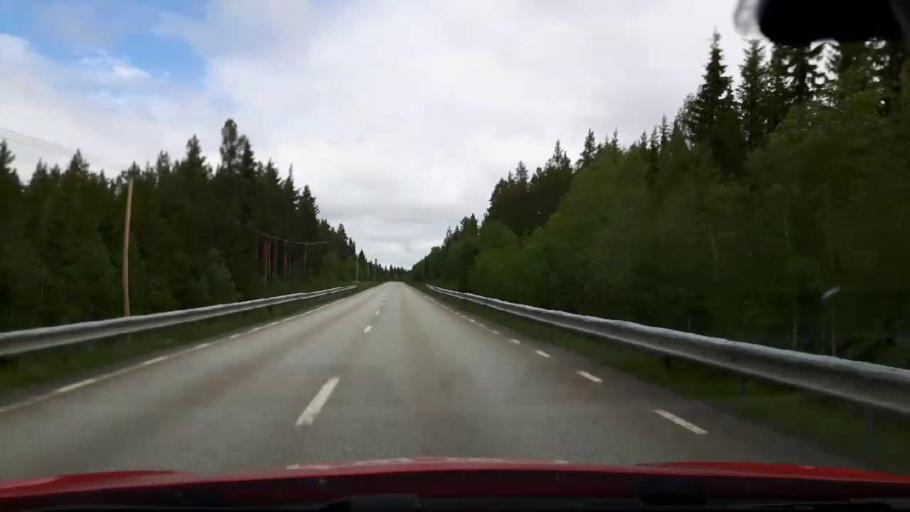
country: SE
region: Jaemtland
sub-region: Krokoms Kommun
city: Krokom
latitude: 63.4629
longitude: 14.4934
